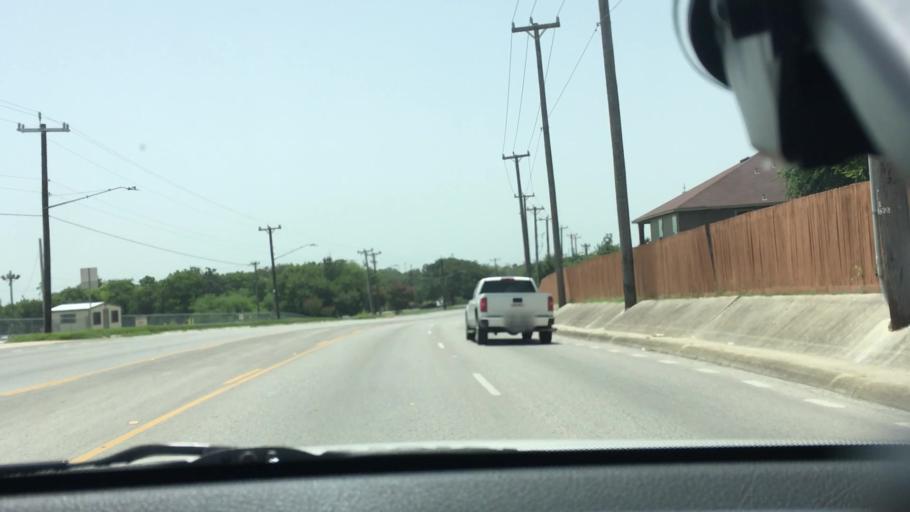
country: US
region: Texas
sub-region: Bexar County
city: Live Oak
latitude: 29.5642
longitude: -98.3527
